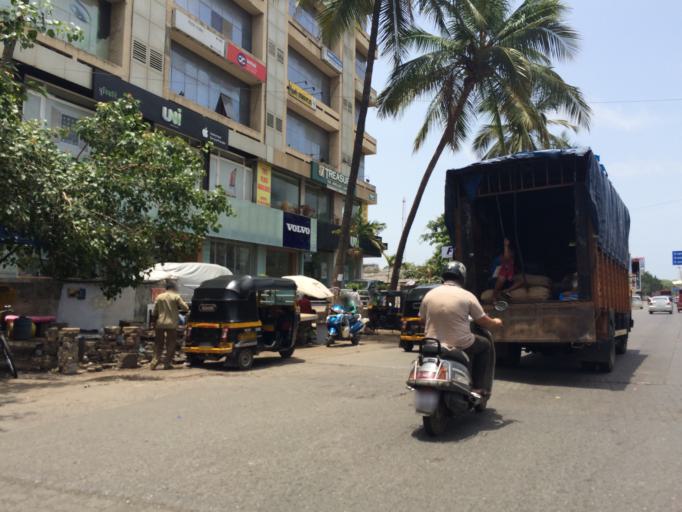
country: IN
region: Maharashtra
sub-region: Mumbai Suburban
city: Powai
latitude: 19.1351
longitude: 72.8321
